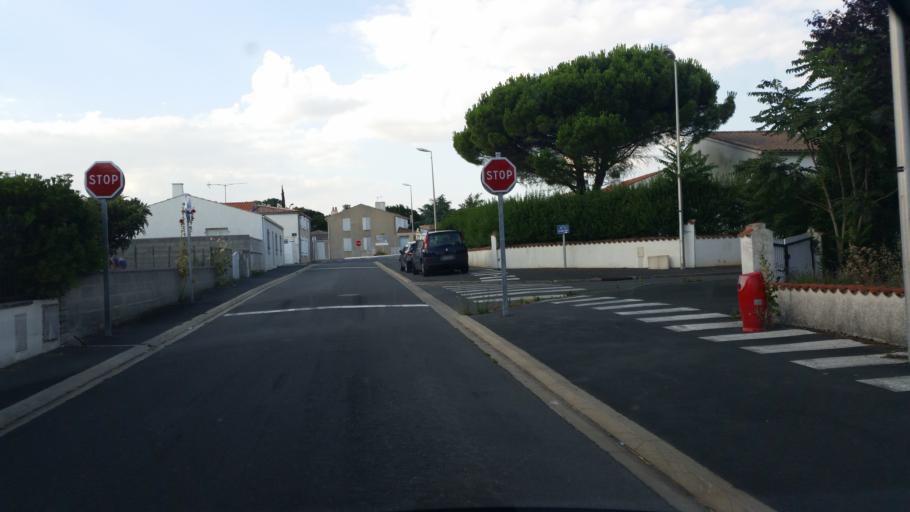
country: FR
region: Poitou-Charentes
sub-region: Departement de la Charente-Maritime
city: Andilly
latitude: 46.2528
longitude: -1.0245
